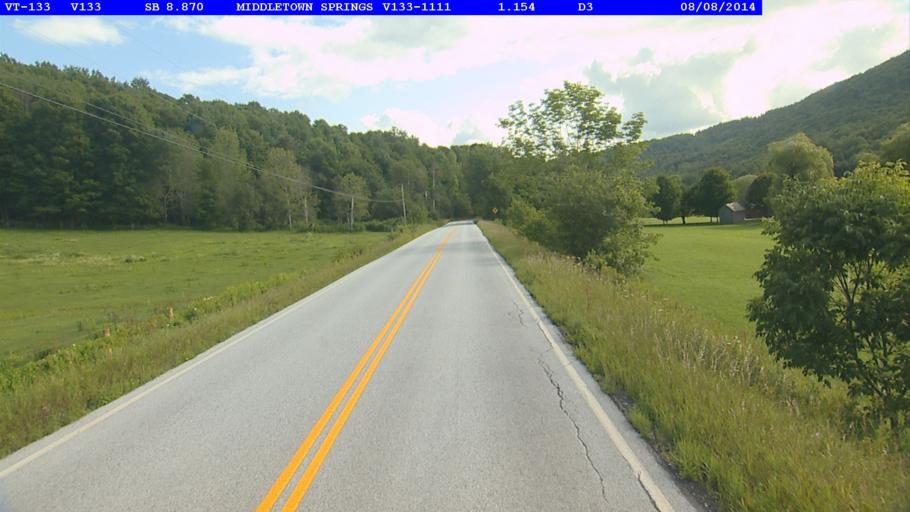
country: US
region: Vermont
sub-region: Rutland County
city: Poultney
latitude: 43.4518
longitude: -73.1090
